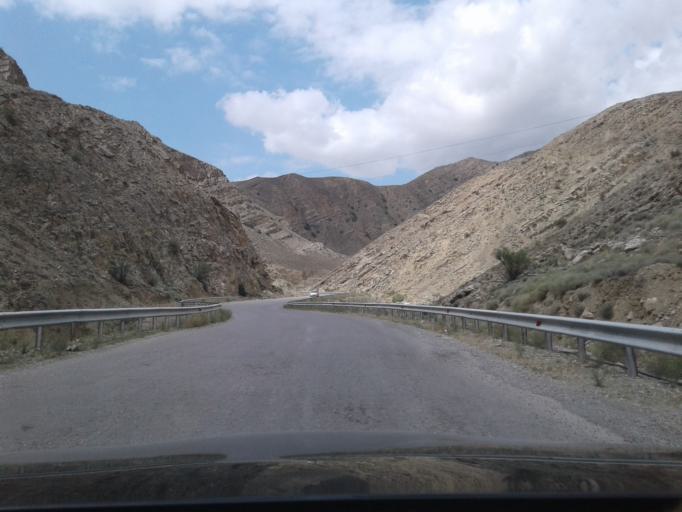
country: TM
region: Ahal
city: Baharly
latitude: 38.5014
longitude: 57.0506
